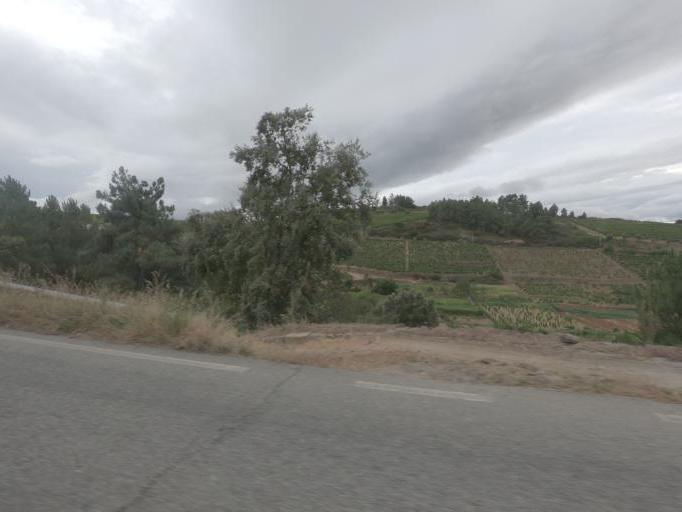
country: PT
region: Vila Real
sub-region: Sabrosa
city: Sabrosa
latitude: 41.2861
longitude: -7.5129
